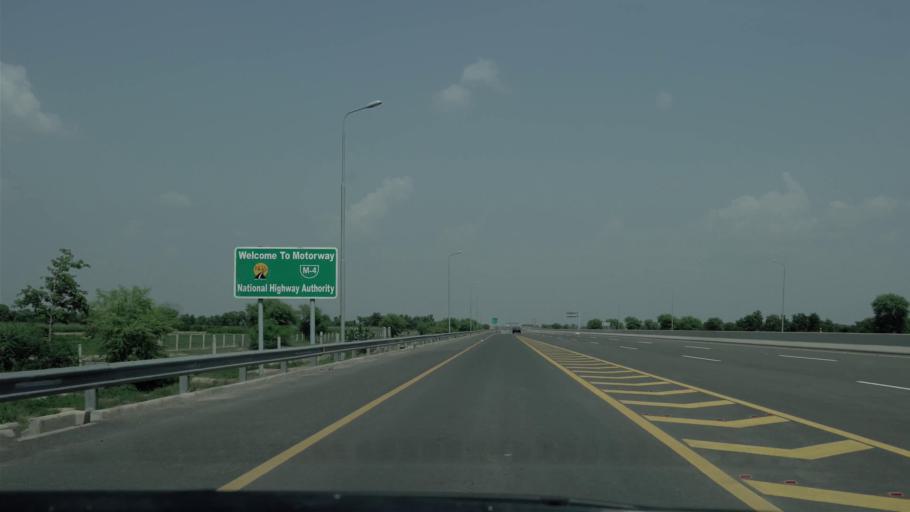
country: PK
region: Punjab
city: Gojra
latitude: 31.1858
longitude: 72.6435
